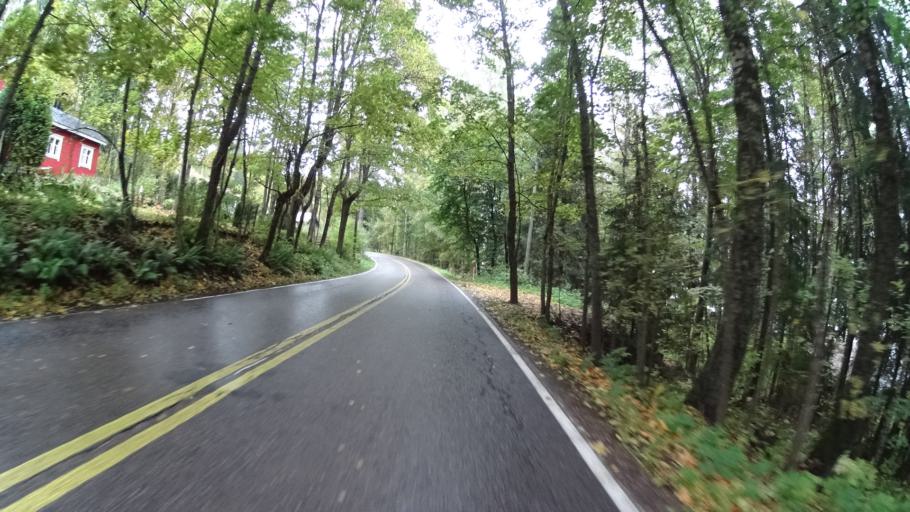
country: FI
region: Uusimaa
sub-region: Helsinki
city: Espoo
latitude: 60.2665
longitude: 24.6554
